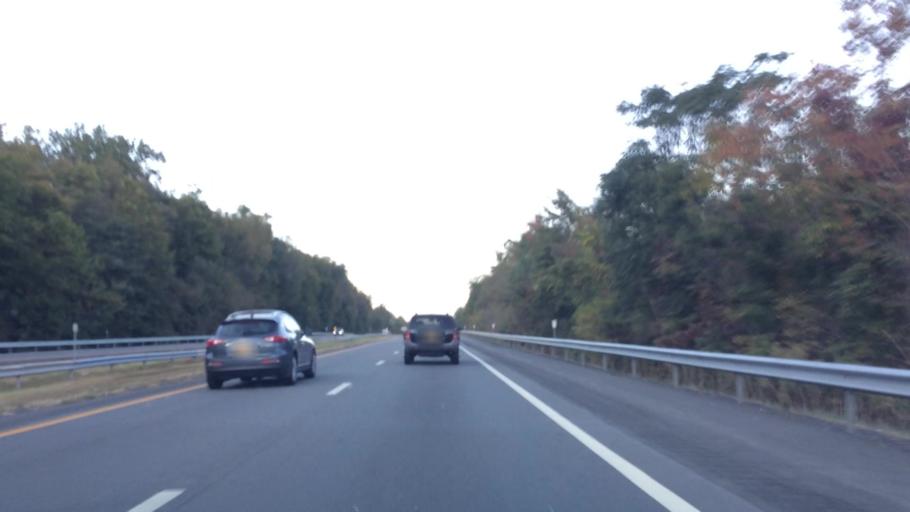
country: US
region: New York
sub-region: Orange County
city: Woodbury
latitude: 41.3843
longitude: -74.1006
